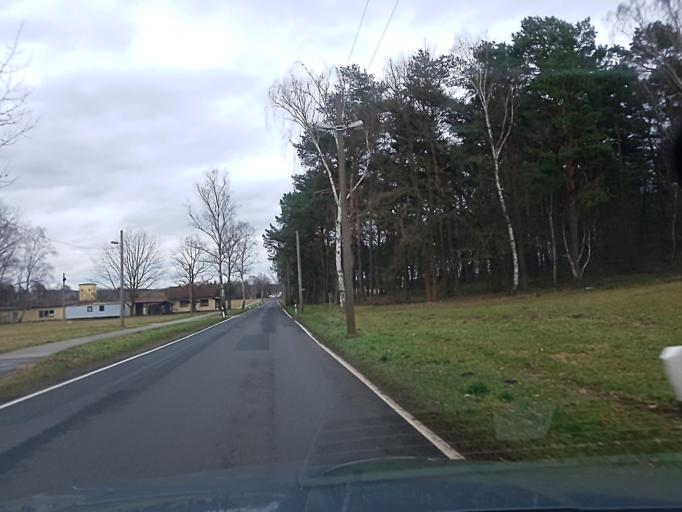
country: DE
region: Brandenburg
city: Bad Liebenwerda
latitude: 51.5577
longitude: 13.4061
